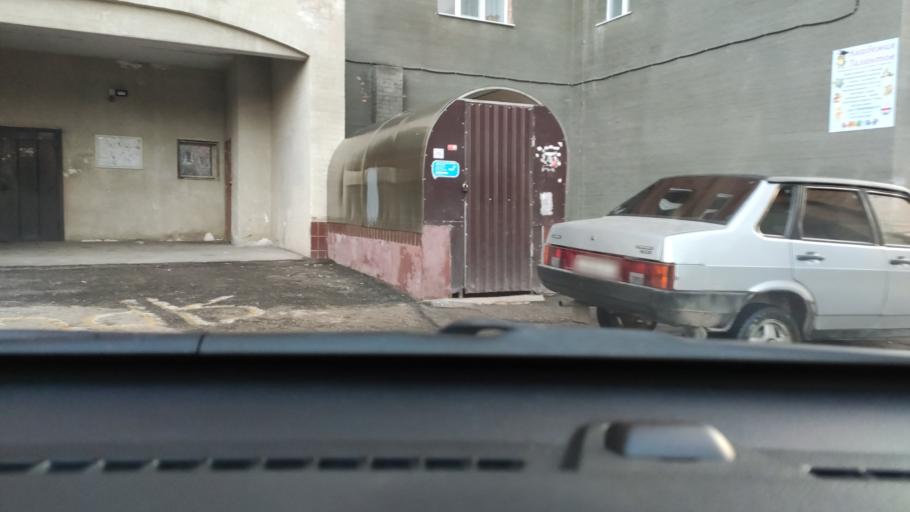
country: RU
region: Samara
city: Podstepki
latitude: 53.5765
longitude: 49.0843
